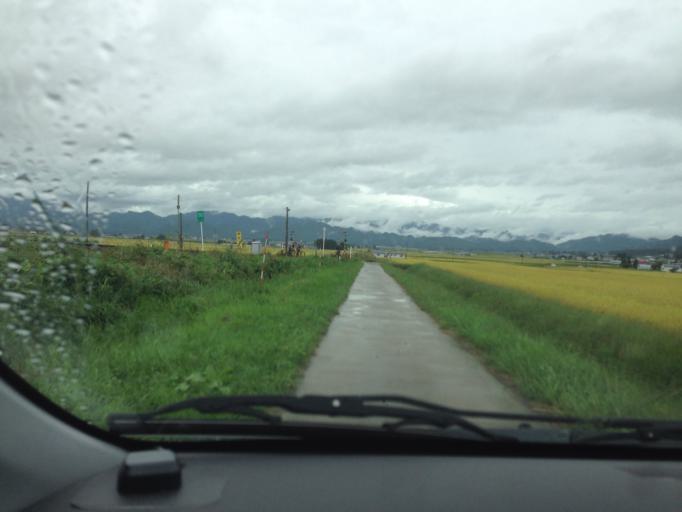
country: JP
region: Fukushima
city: Kitakata
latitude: 37.5070
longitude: 139.8286
